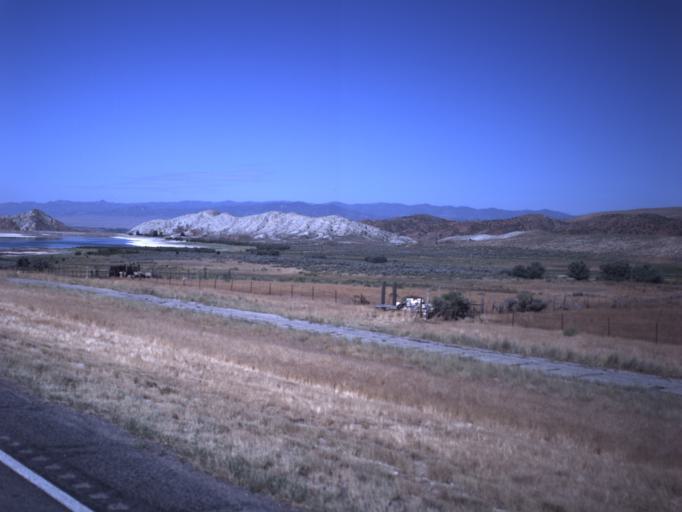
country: US
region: Utah
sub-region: Sanpete County
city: Manti
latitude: 39.1838
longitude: -111.6965
